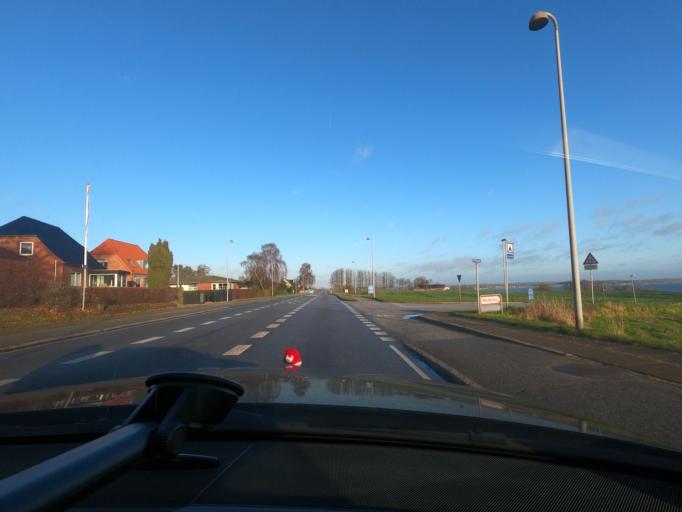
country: DK
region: South Denmark
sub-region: Sonderborg Kommune
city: Grasten
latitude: 54.8973
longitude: 9.5600
